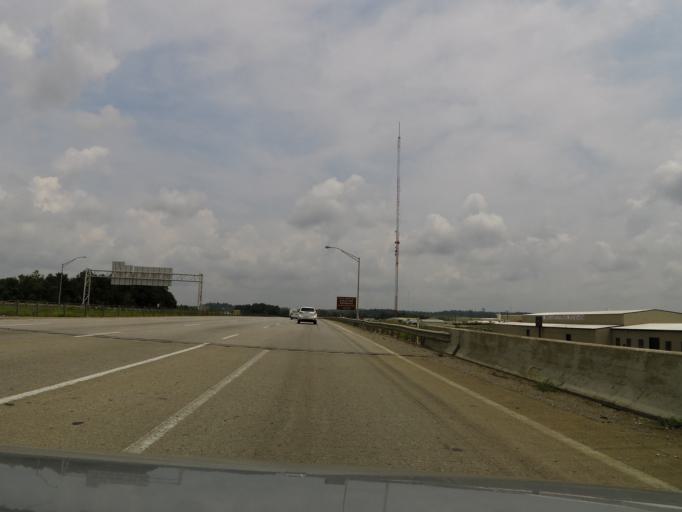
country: US
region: Kentucky
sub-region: Hardin County
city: Elizabethtown
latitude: 37.6790
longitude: -85.8457
